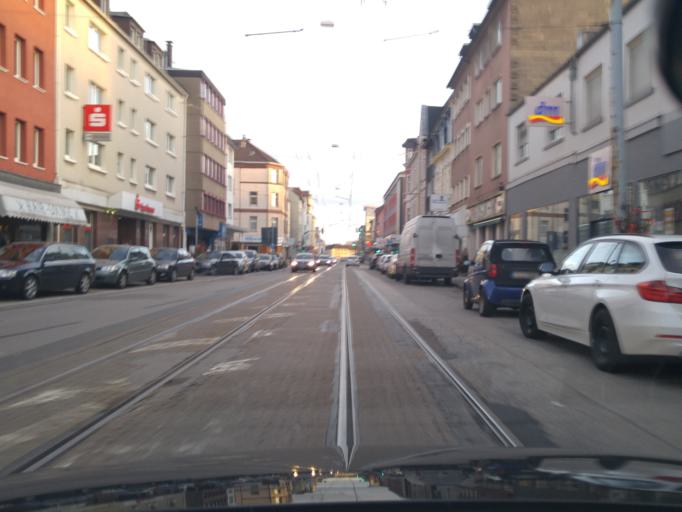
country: DE
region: North Rhine-Westphalia
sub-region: Regierungsbezirk Dusseldorf
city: Essen
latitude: 51.4507
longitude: 7.0309
